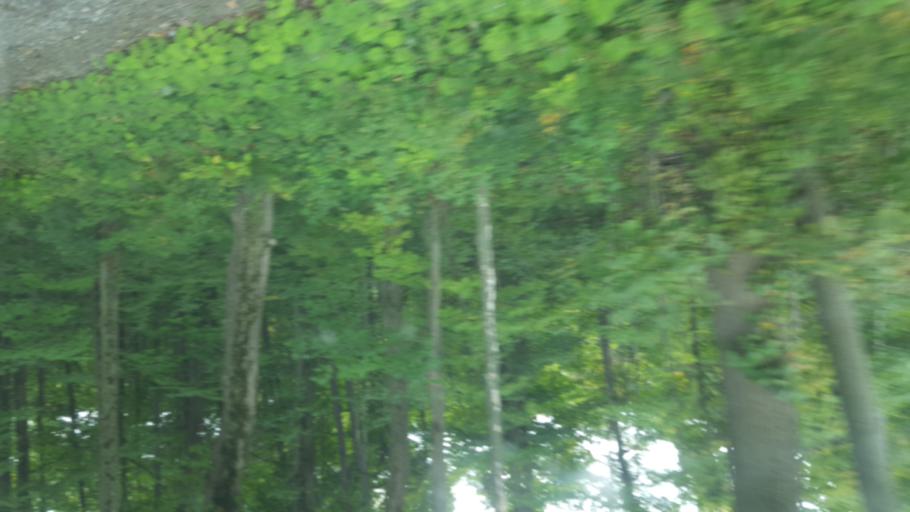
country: US
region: Pennsylvania
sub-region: Crawford County
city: Pymatuning Central
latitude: 41.5262
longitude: -80.3967
